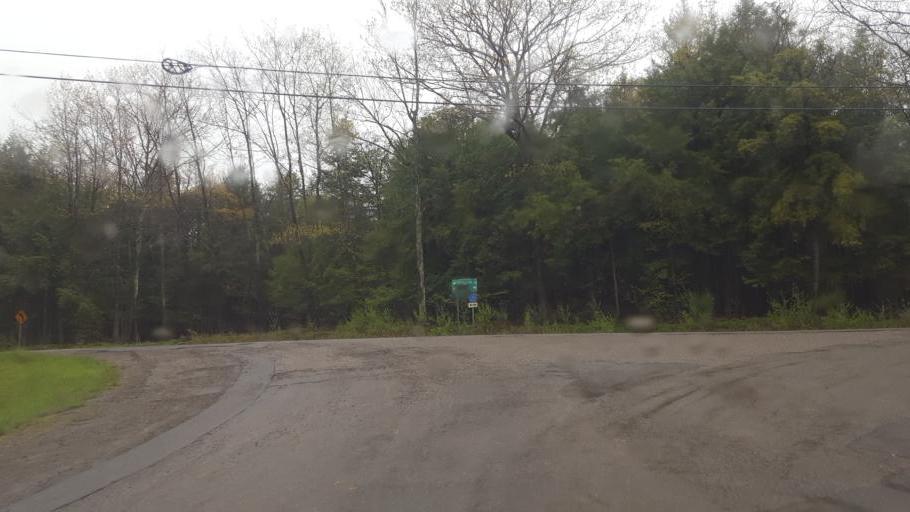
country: US
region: Pennsylvania
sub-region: Tioga County
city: Elkland
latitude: 42.0376
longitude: -77.4163
